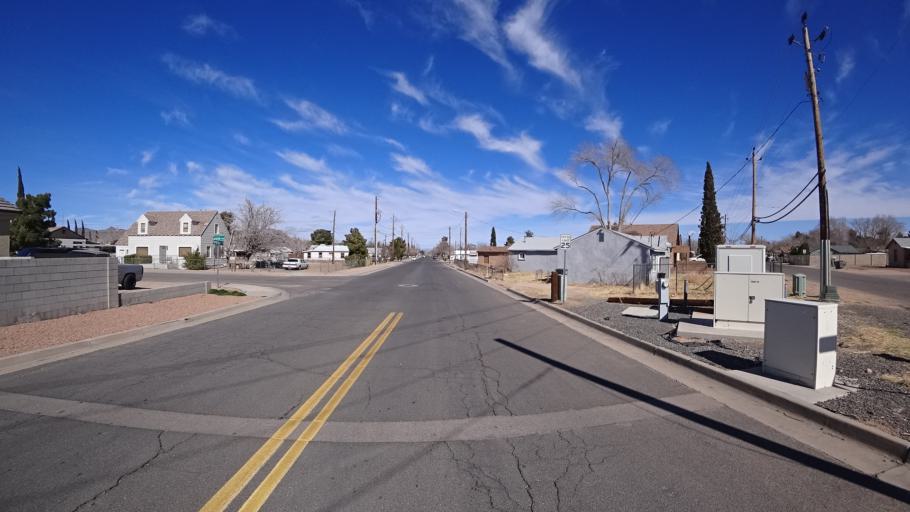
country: US
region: Arizona
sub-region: Mohave County
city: Kingman
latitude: 35.1993
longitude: -114.0292
